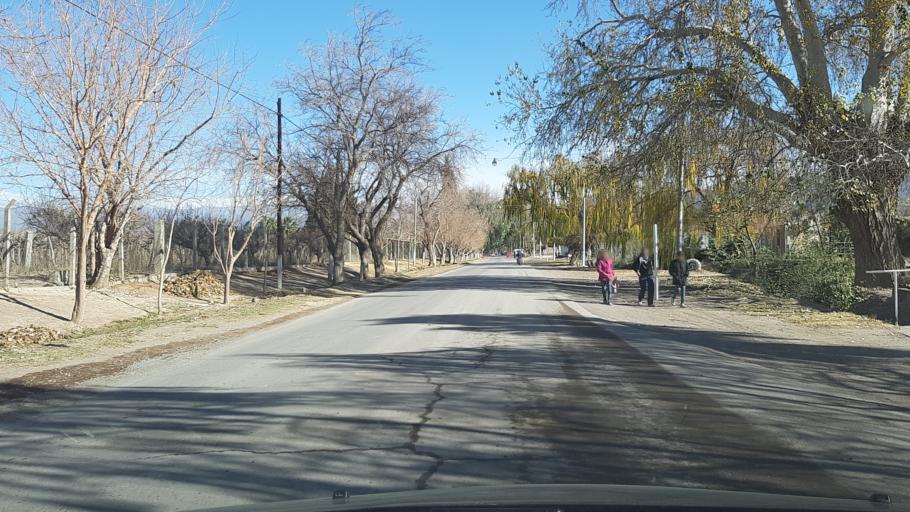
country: AR
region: San Juan
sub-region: Departamento de Zonda
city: Zonda
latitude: -31.4610
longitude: -68.7307
